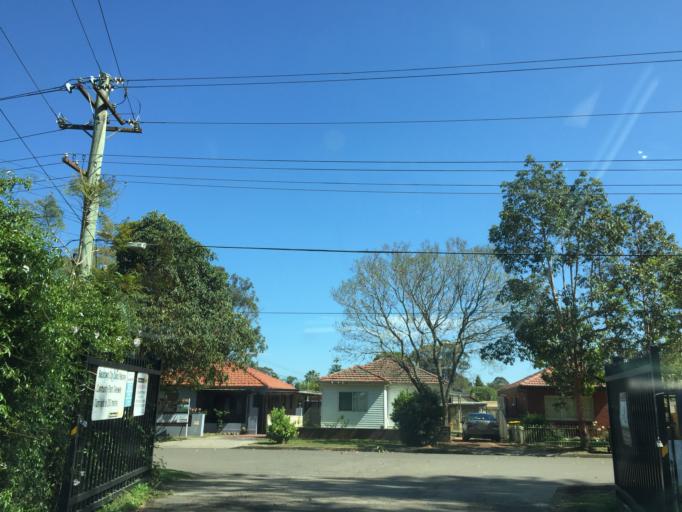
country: AU
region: New South Wales
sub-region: Blacktown
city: Blacktown
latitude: -33.7653
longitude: 150.8983
